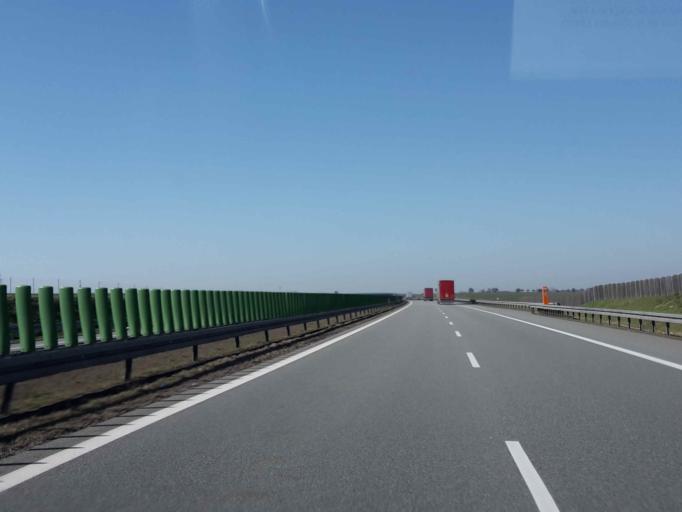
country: PL
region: Greater Poland Voivodeship
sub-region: Powiat nowotomyski
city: Kuslin
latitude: 52.3765
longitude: 16.2465
